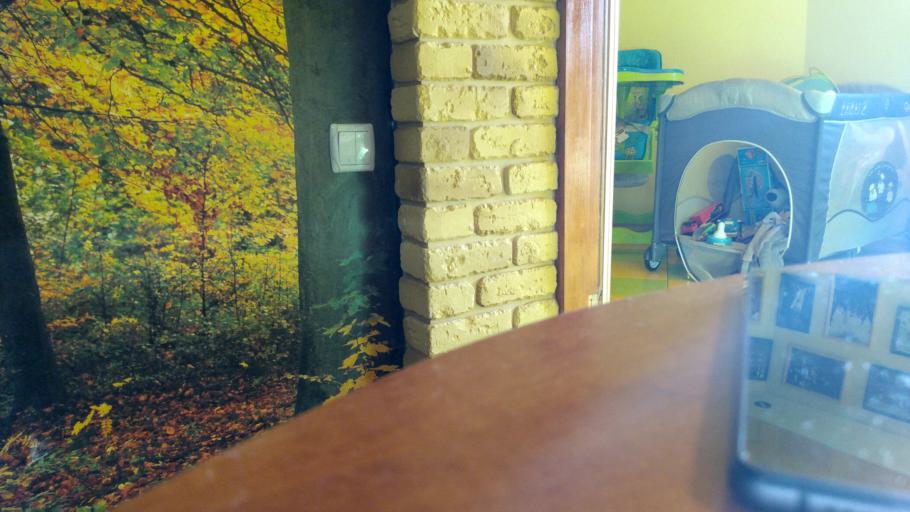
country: RU
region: Tverskaya
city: Likhoslavl'
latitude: 57.1360
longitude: 35.6340
